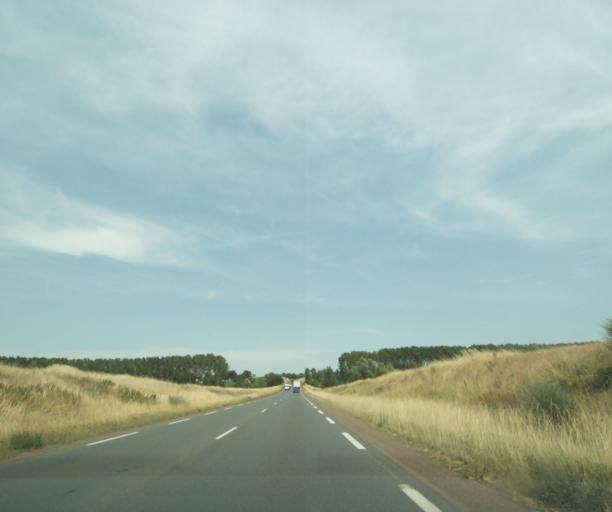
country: FR
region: Poitou-Charentes
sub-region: Departement de la Vienne
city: Cenon-sur-Vienne
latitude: 46.7878
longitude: 0.5498
